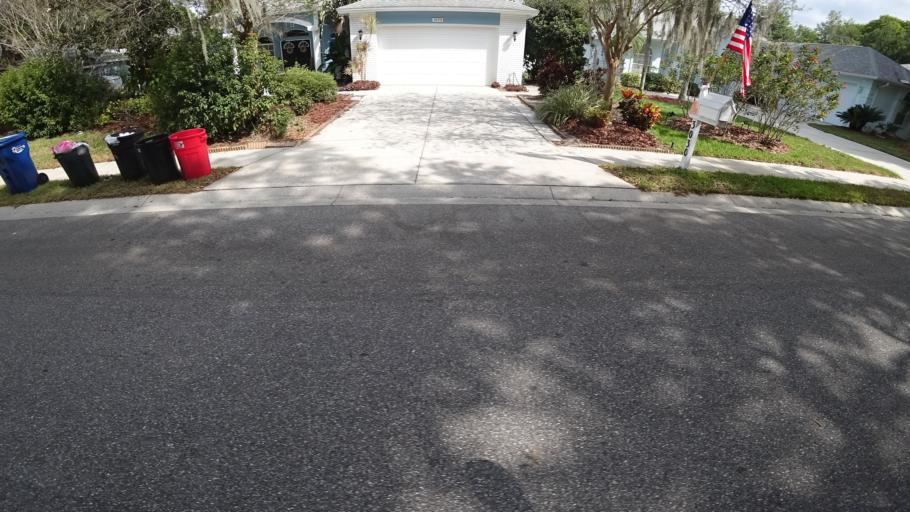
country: US
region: Florida
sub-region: Manatee County
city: Ellenton
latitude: 27.5403
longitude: -82.4499
